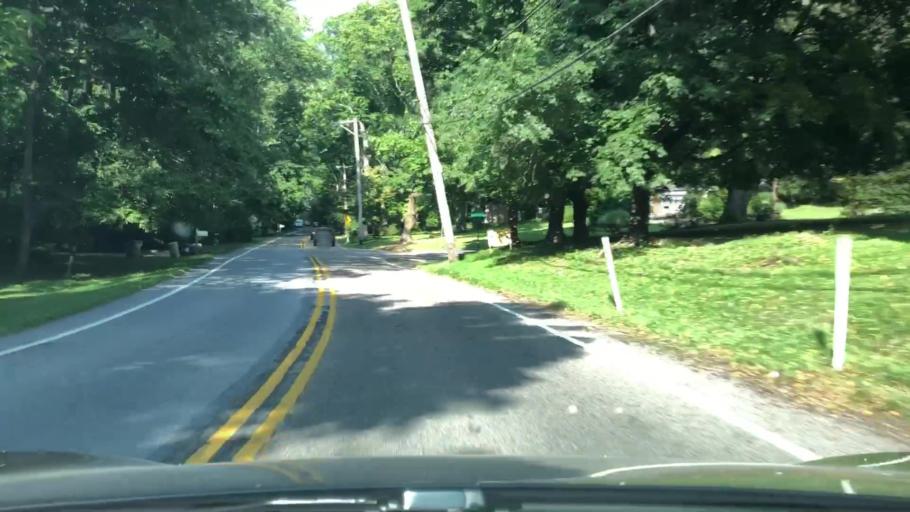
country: US
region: Pennsylvania
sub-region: Delaware County
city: Broomall
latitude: 39.9983
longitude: -75.3902
